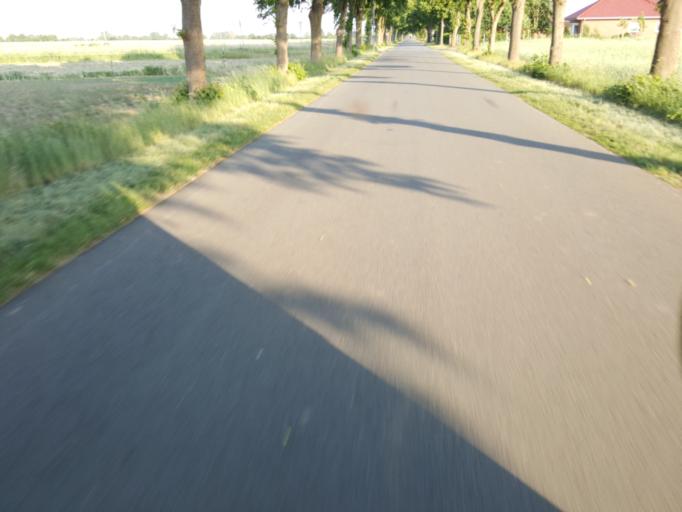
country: DE
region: Lower Saxony
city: Landesbergen
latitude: 52.5488
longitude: 9.1414
